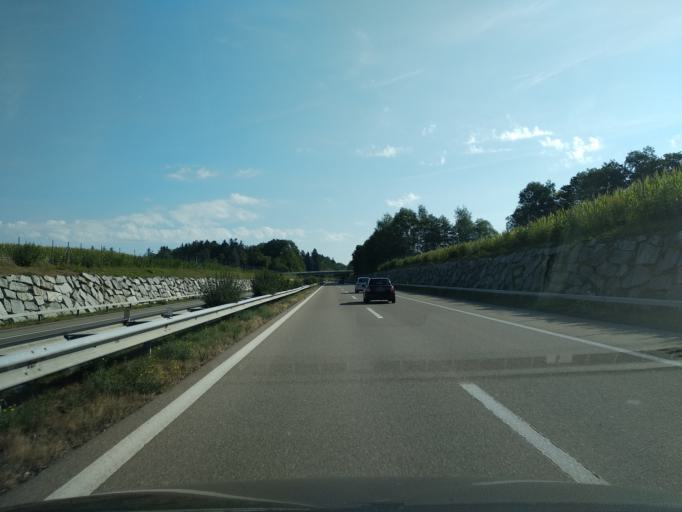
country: CH
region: Thurgau
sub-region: Kreuzlingen District
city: Tagerwilen
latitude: 47.6187
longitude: 9.1115
